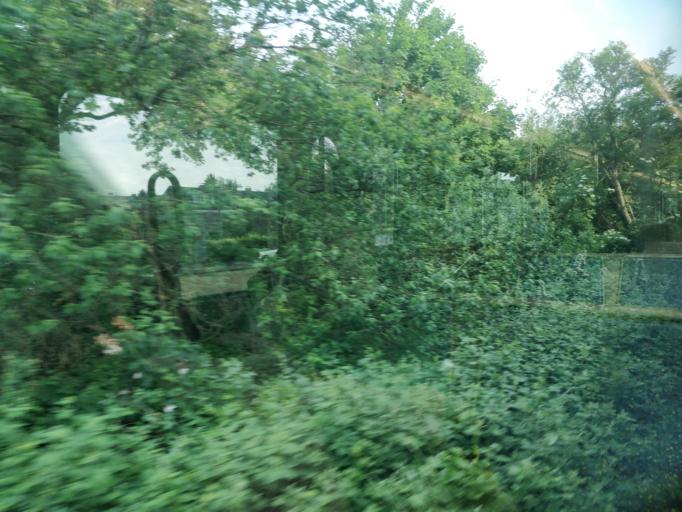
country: DE
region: North Rhine-Westphalia
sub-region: Regierungsbezirk Koln
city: Bilderstoeckchen
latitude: 50.9714
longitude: 6.9050
